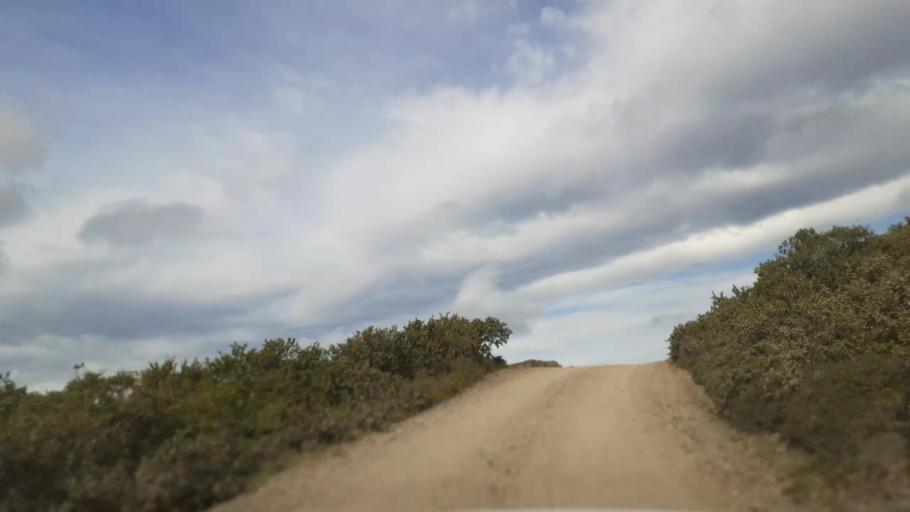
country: IS
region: East
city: Hoefn
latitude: 64.4397
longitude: -14.9194
